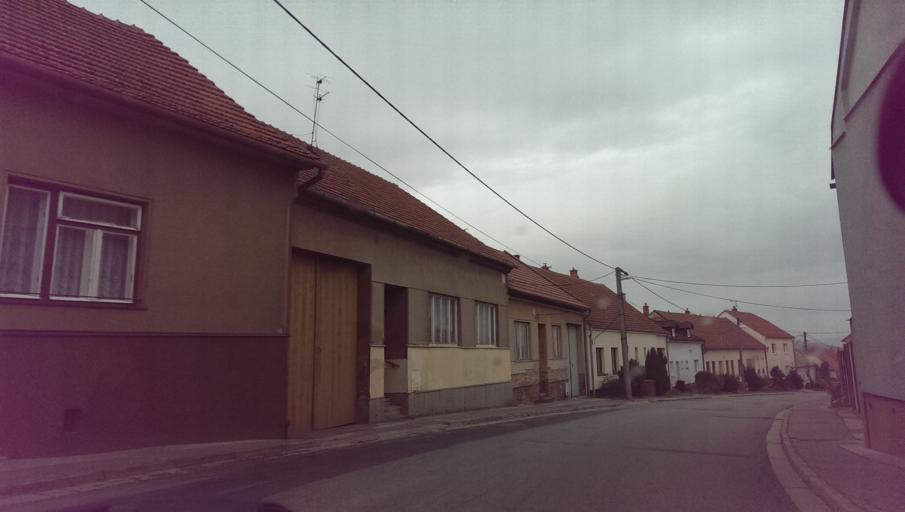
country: CZ
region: South Moravian
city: Ostopovice
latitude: 49.1410
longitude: 16.5529
